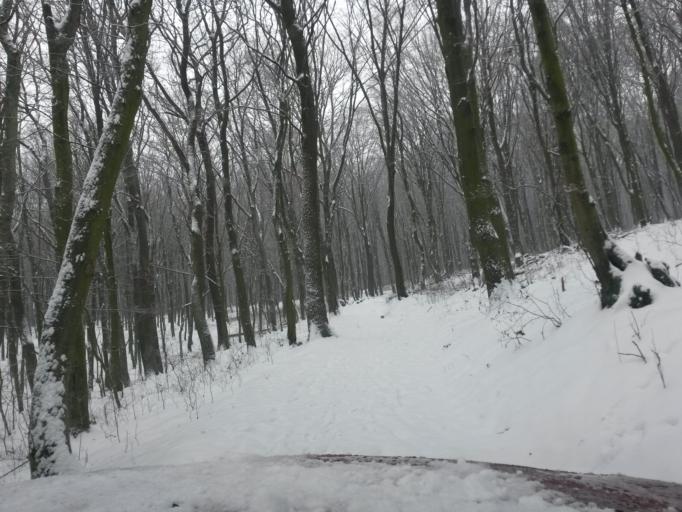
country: SK
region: Kosicky
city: Kosice
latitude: 48.7204
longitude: 21.3085
